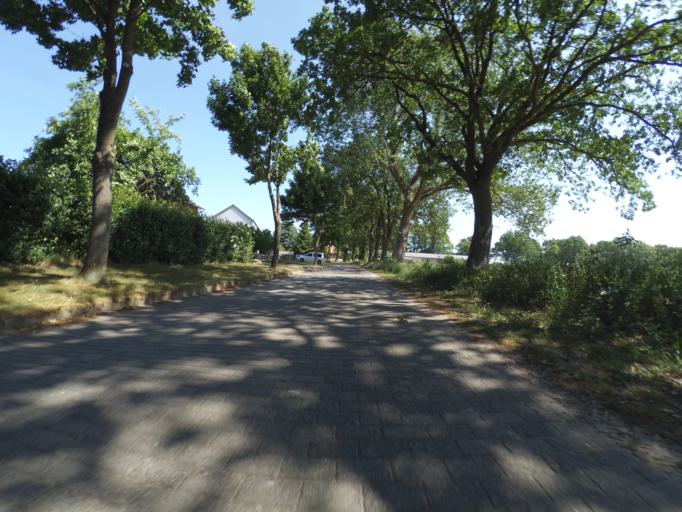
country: DE
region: Brandenburg
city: Heiligengrabe
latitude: 53.1996
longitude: 12.3324
